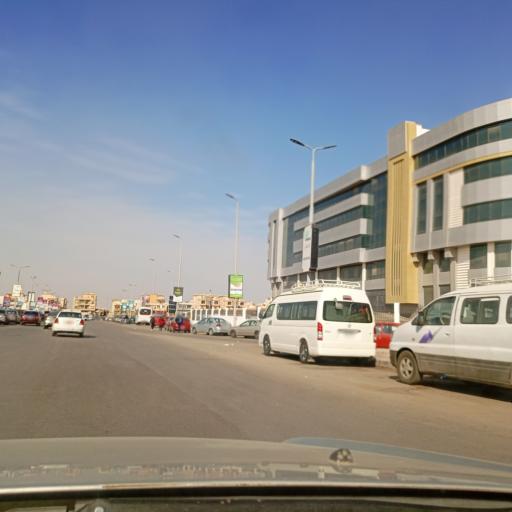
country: EG
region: Muhafazat al Qahirah
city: Cairo
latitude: 30.0188
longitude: 31.4328
